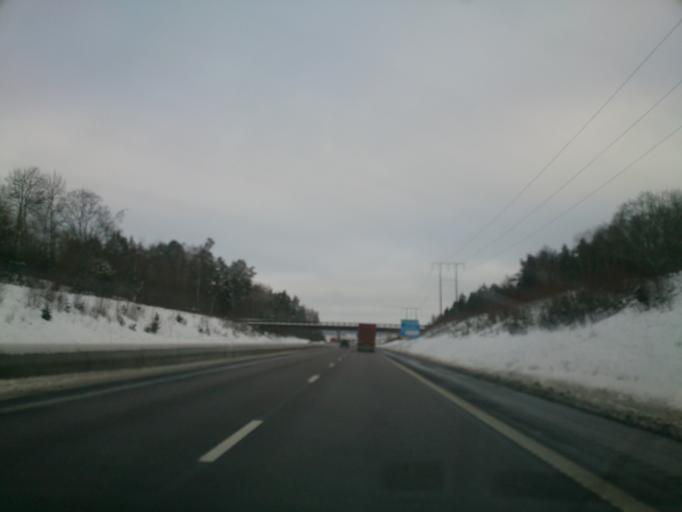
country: SE
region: OEstergoetland
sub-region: Norrkopings Kommun
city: Norrkoping
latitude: 58.6133
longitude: 16.1393
